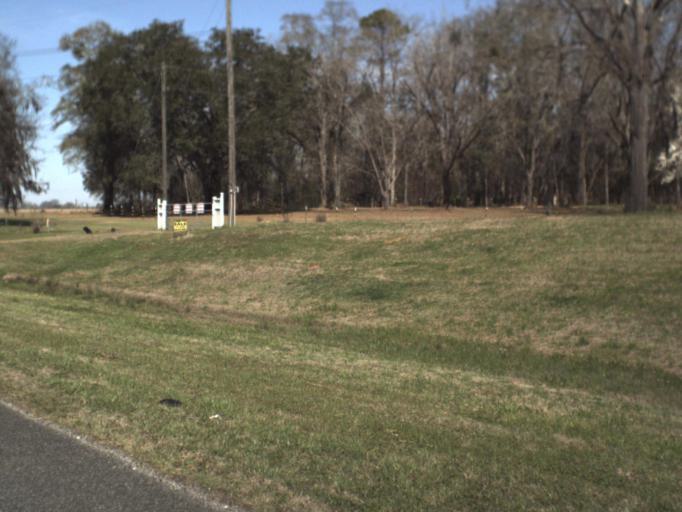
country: US
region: Florida
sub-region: Jackson County
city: Graceville
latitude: 30.9190
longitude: -85.3819
